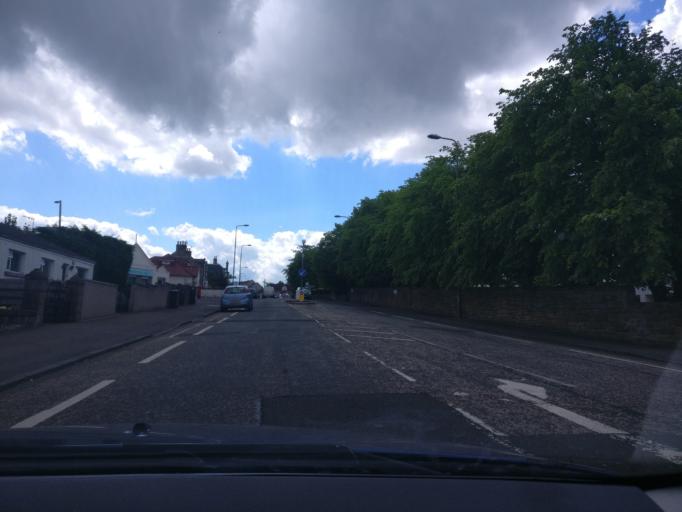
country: GB
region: Scotland
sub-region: Midlothian
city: Loanhead
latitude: 55.9074
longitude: -3.1350
